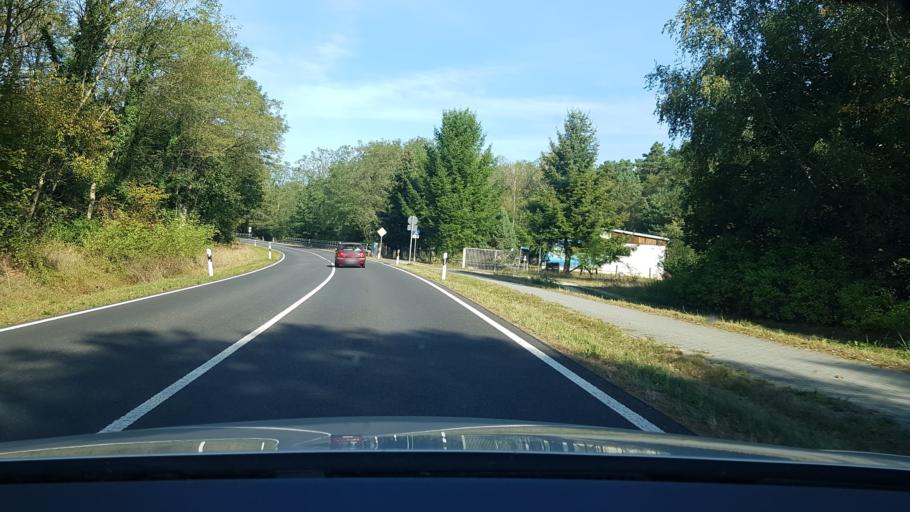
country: DE
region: Brandenburg
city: Mixdorf
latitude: 52.1459
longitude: 14.4156
